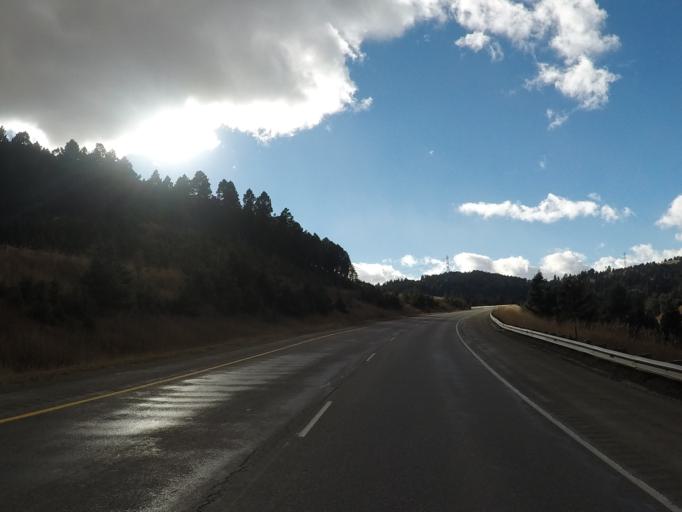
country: US
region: Montana
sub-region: Jefferson County
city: Boulder
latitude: 46.3301
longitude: -112.0572
